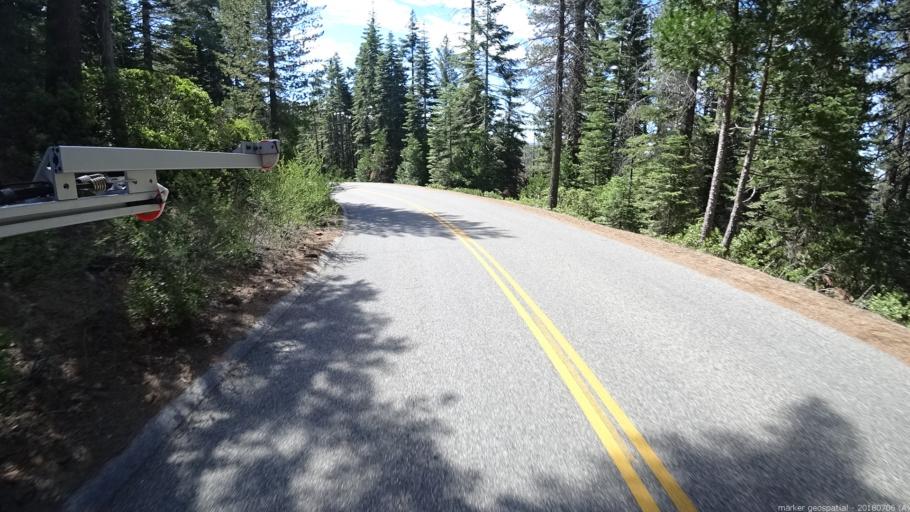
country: US
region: California
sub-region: Madera County
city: Oakhurst
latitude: 37.3874
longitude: -119.5246
